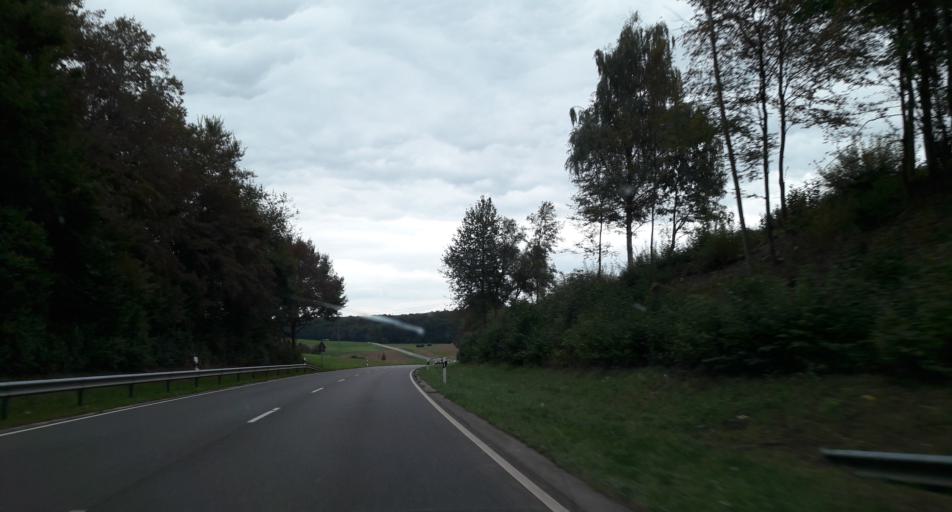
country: DE
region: Baden-Wuerttemberg
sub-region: Regierungsbezirk Stuttgart
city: Kirchardt
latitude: 49.2216
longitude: 8.9644
